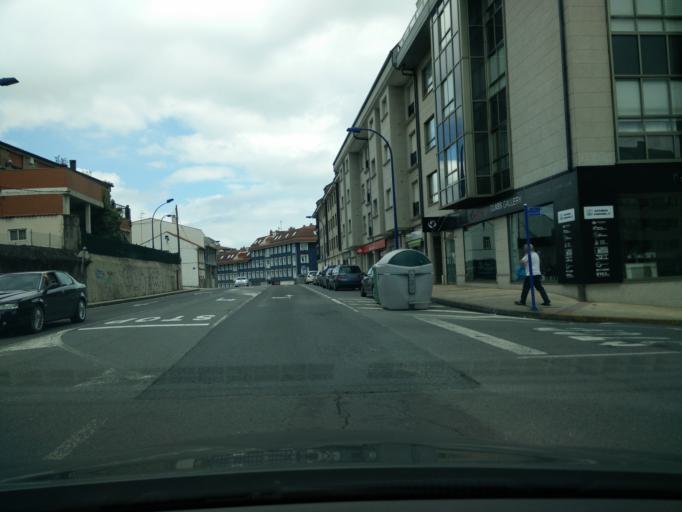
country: ES
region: Galicia
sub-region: Provincia da Coruna
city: Culleredo
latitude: 43.3222
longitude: -8.3836
